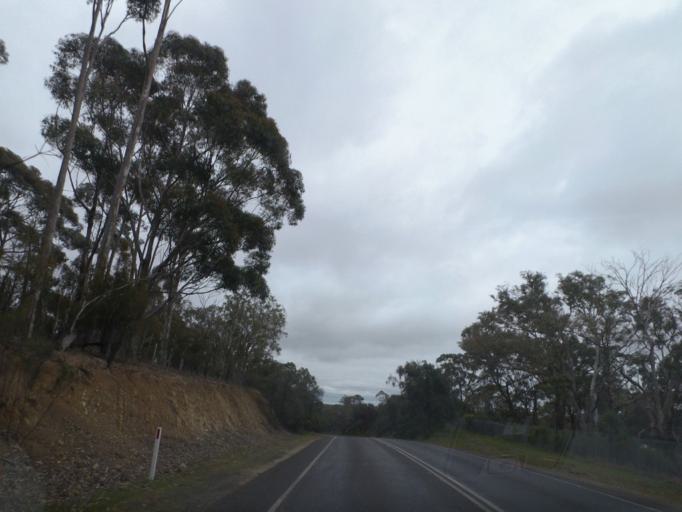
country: AU
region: Victoria
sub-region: Nillumbik
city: Doreen
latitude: -37.5700
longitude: 145.1267
